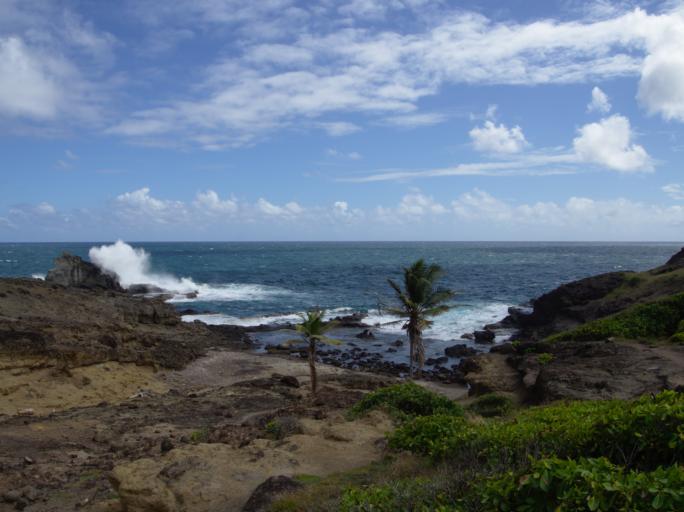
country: MQ
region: Martinique
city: Petite Riviere Salee
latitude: 14.7715
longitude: -60.8746
